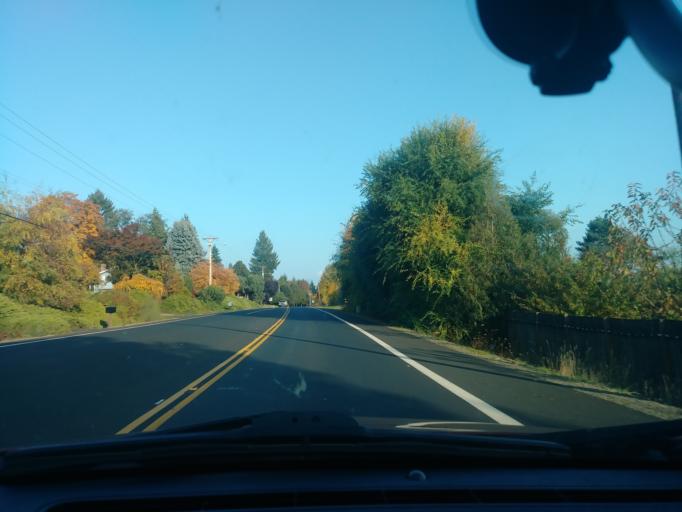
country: US
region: Oregon
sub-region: Washington County
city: Forest Grove
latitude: 45.5301
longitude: -123.1368
